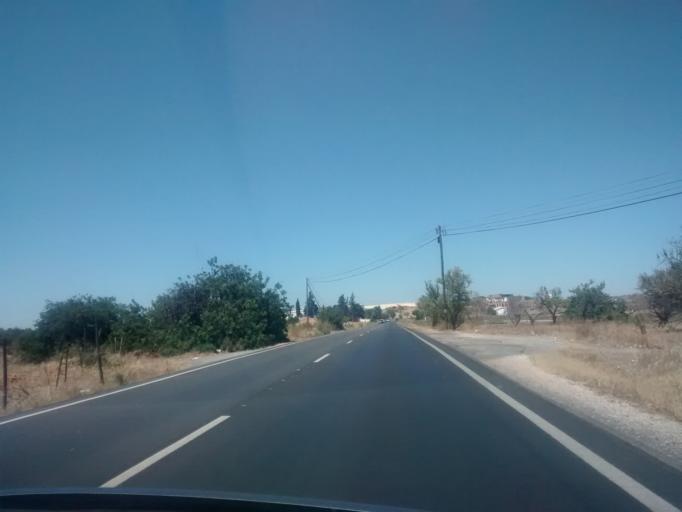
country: PT
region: Faro
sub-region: Castro Marim
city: Castro Marim
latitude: 37.2066
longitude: -7.4345
